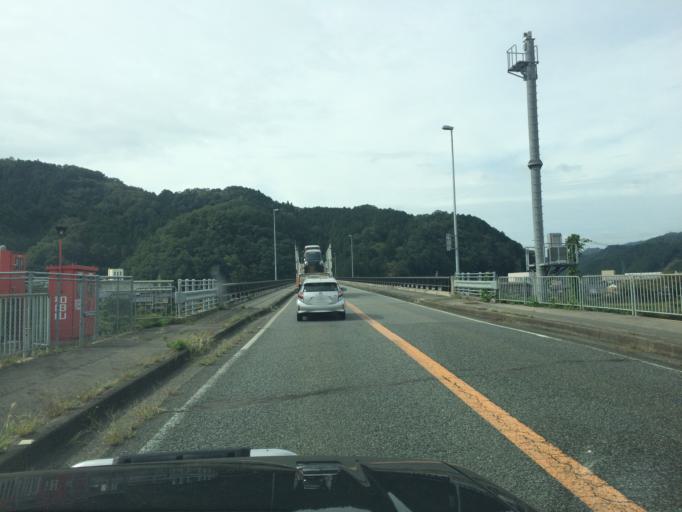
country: JP
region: Hyogo
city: Toyooka
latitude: 35.3341
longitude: 134.8596
